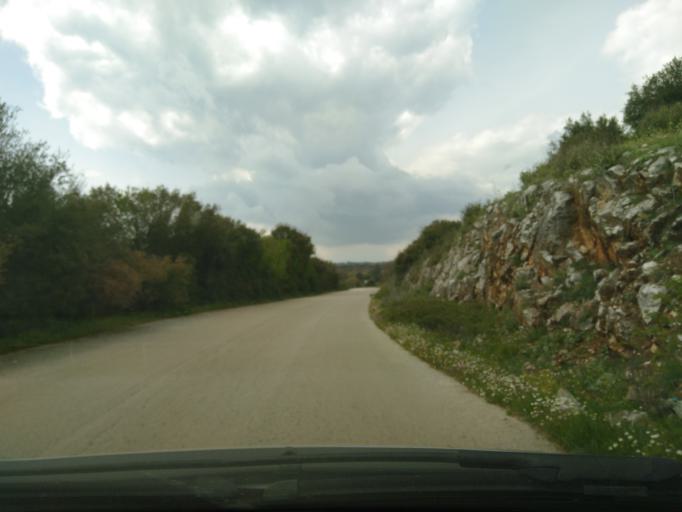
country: GR
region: Epirus
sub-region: Nomos Ioanninon
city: Asprangeloi
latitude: 39.7744
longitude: 20.6903
